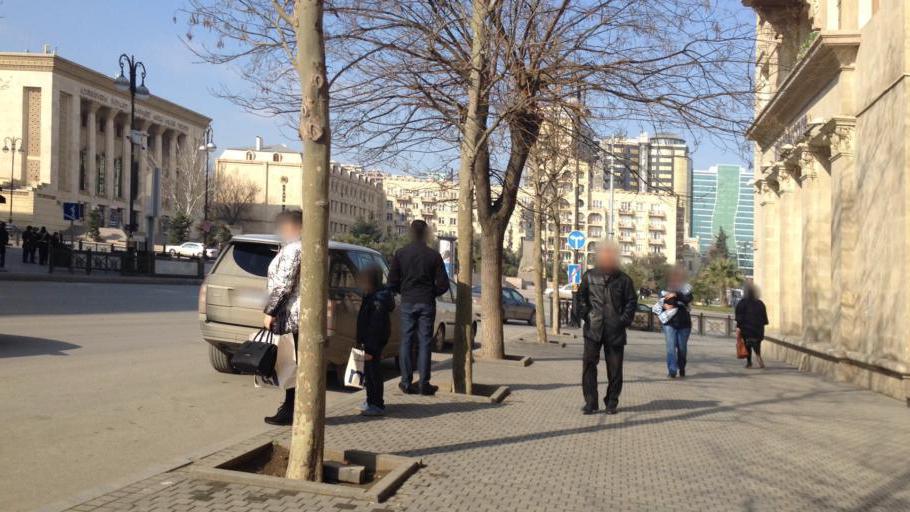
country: AZ
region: Baki
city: Badamdar
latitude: 40.3744
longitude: 49.8326
